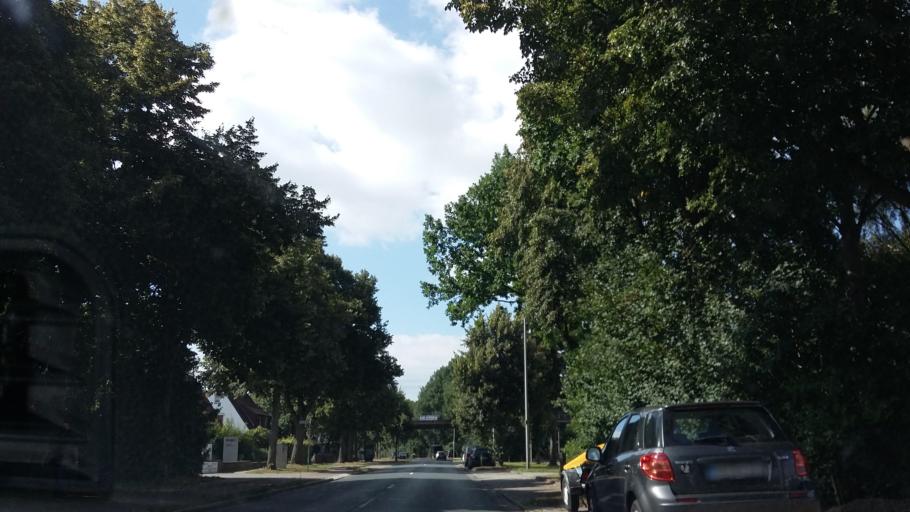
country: DE
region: Bremen
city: Bremen
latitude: 53.0428
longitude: 8.8272
